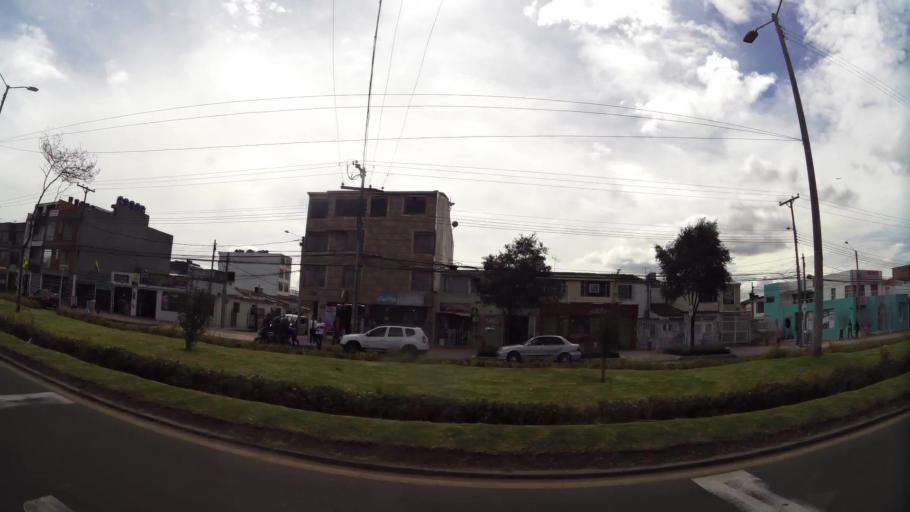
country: CO
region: Bogota D.C.
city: Bogota
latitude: 4.6241
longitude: -74.1367
